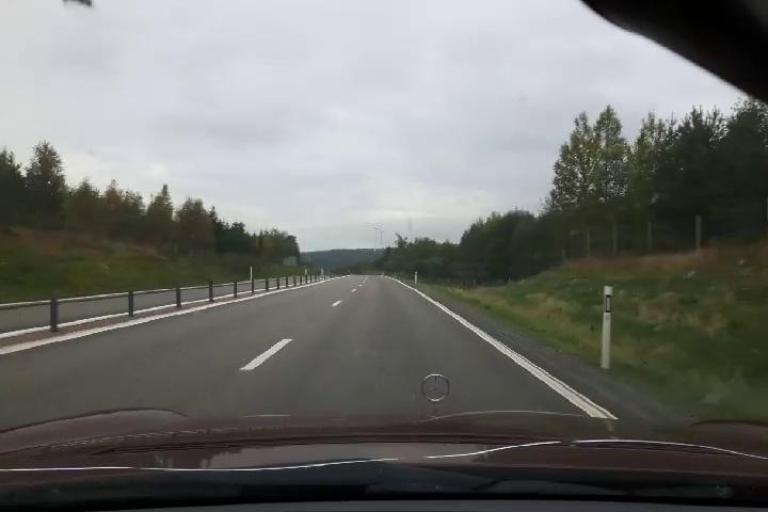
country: SE
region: Vaesternorrland
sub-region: Haernoesands Kommun
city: Haernoesand
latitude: 62.7625
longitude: 17.9060
